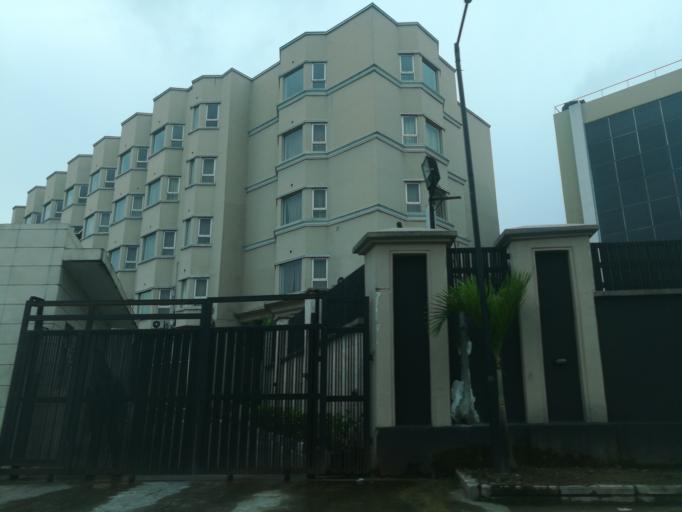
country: NG
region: Rivers
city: Port Harcourt
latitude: 4.8229
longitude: 6.9925
